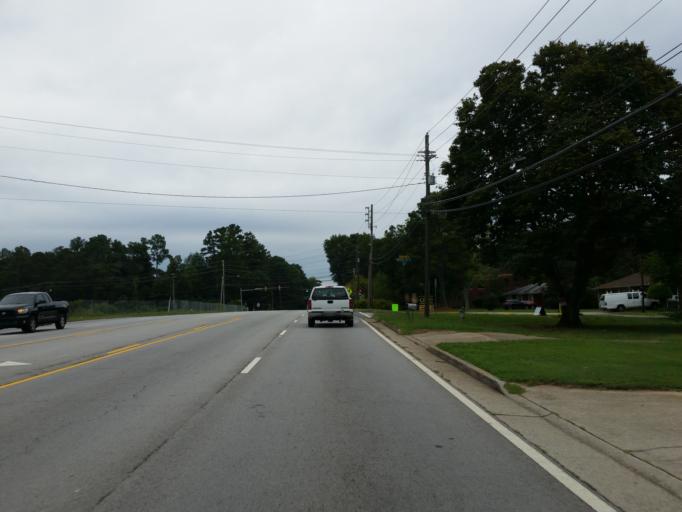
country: US
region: Georgia
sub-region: Cobb County
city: Fair Oaks
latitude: 33.8950
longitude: -84.6095
